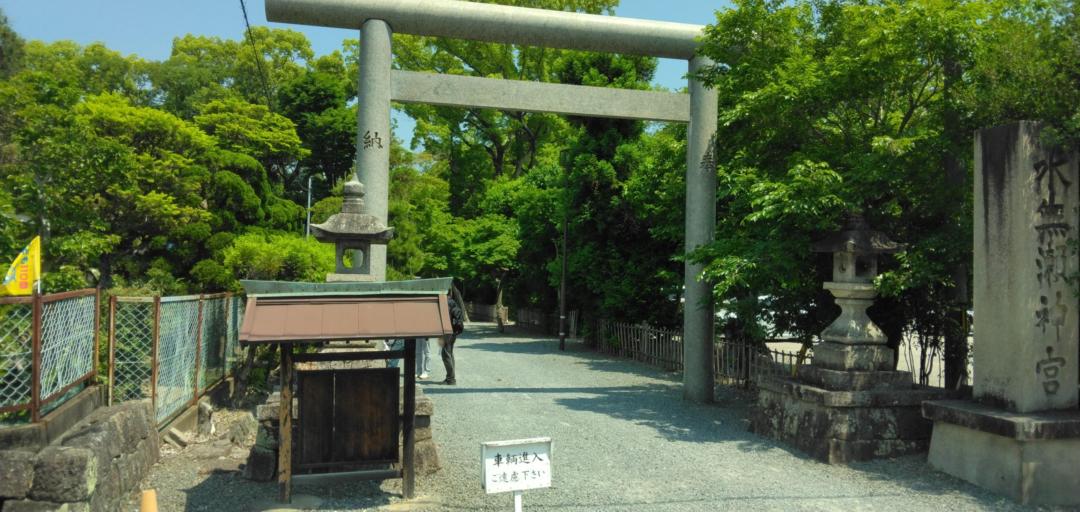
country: JP
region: Kyoto
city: Yawata
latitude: 34.8852
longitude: 135.6719
